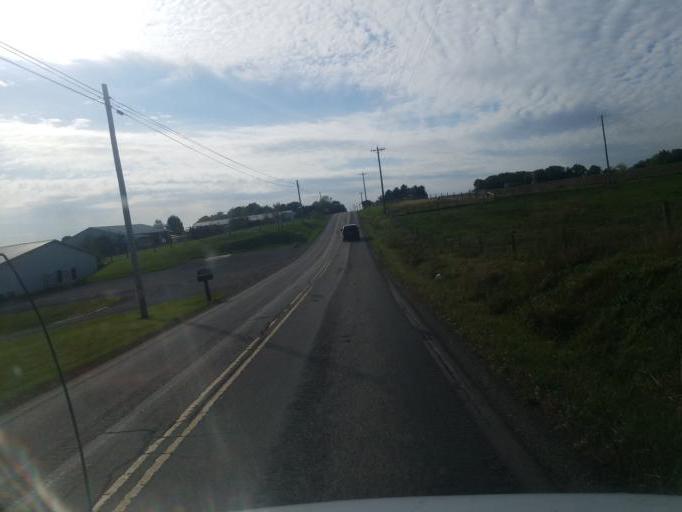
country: US
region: Ohio
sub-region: Wayne County
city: Apple Creek
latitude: 40.6897
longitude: -81.8367
